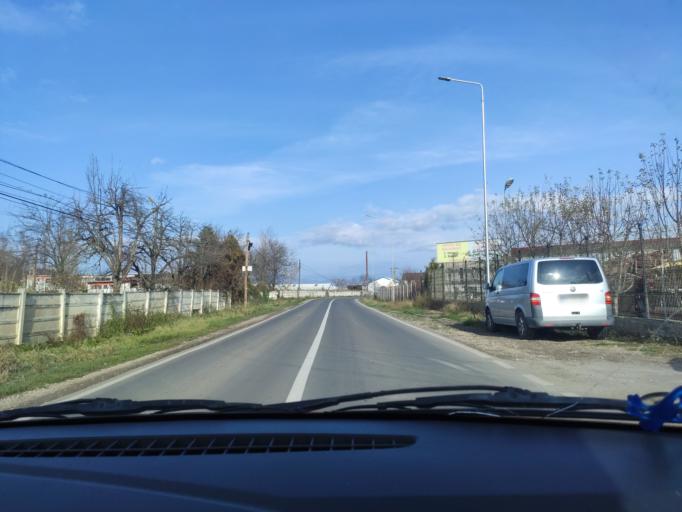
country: RO
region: Brasov
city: Codlea
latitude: 45.7076
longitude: 25.4598
